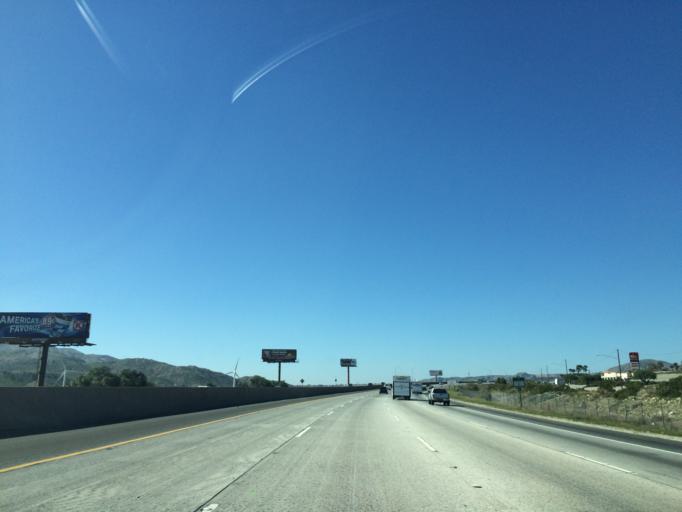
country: US
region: California
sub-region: Riverside County
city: Cabazon
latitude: 33.9189
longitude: -116.7979
